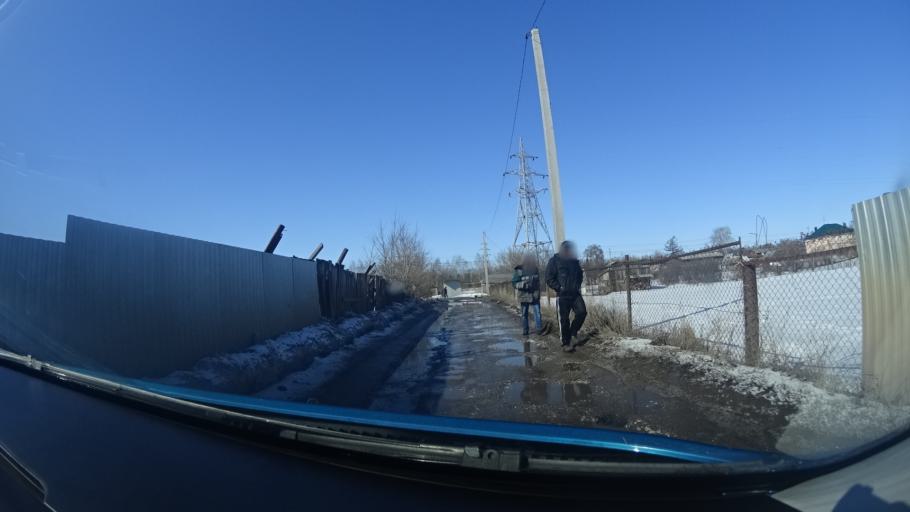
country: RU
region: Bashkortostan
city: Chishmy
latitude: 54.5787
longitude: 55.3742
